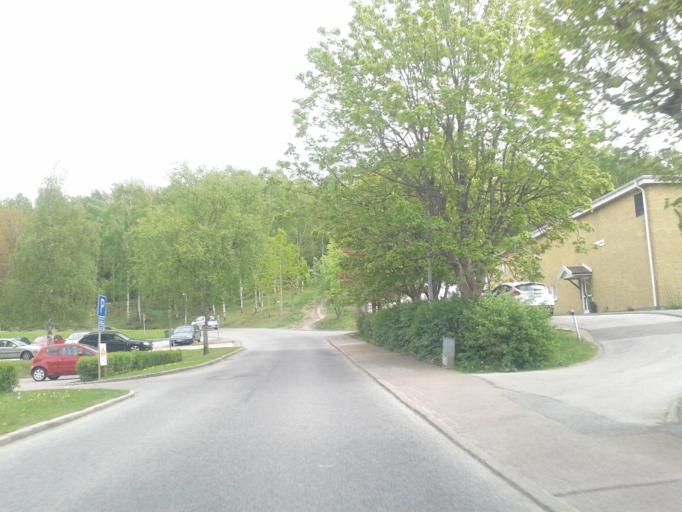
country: SE
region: Vaestra Goetaland
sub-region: Kungalvs Kommun
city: Kungalv
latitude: 57.8761
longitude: 11.9940
